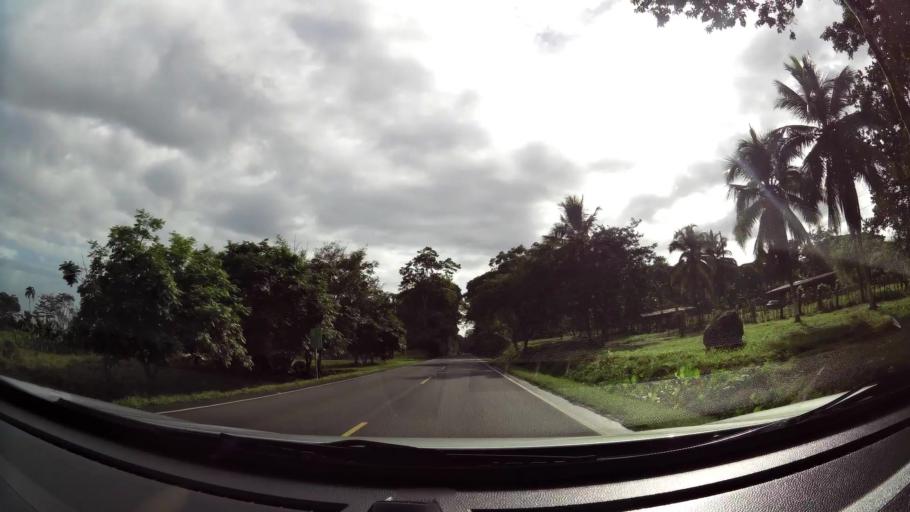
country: CR
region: Limon
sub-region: Canton de Guacimo
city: Guacimo
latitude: 10.2054
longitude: -83.7292
